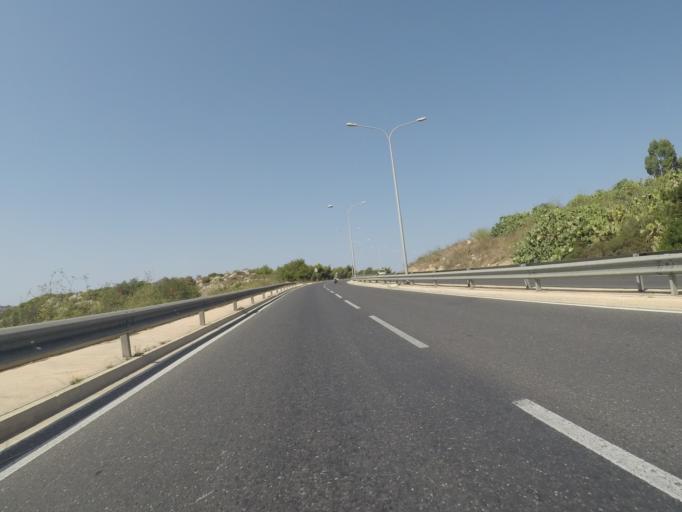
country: MT
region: Saint Paul's Bay
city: San Pawl il-Bahar
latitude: 35.9441
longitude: 14.3917
